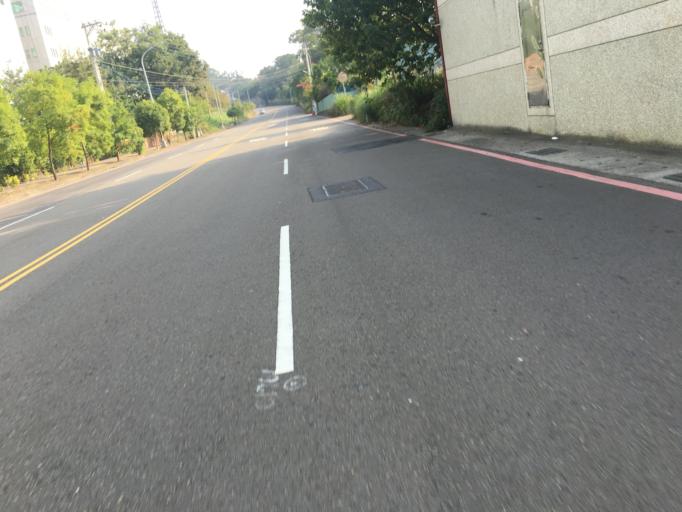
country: TW
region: Taiwan
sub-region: Hsinchu
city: Hsinchu
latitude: 24.7613
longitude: 121.0190
